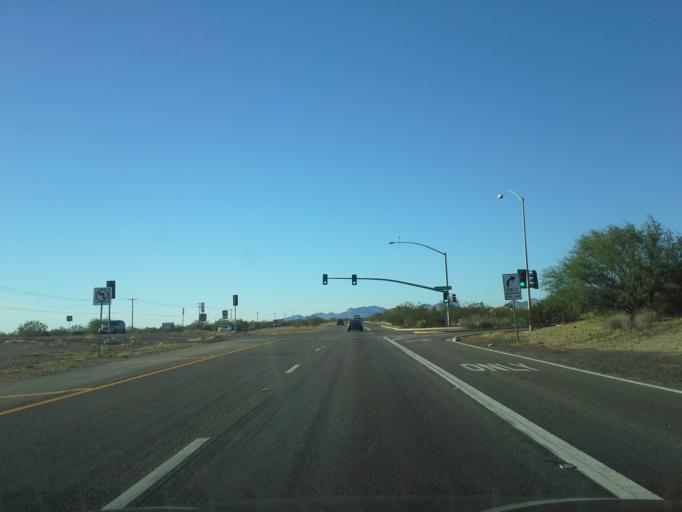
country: US
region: Arizona
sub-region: Pinal County
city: Apache Junction
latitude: 33.3355
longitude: -111.4397
